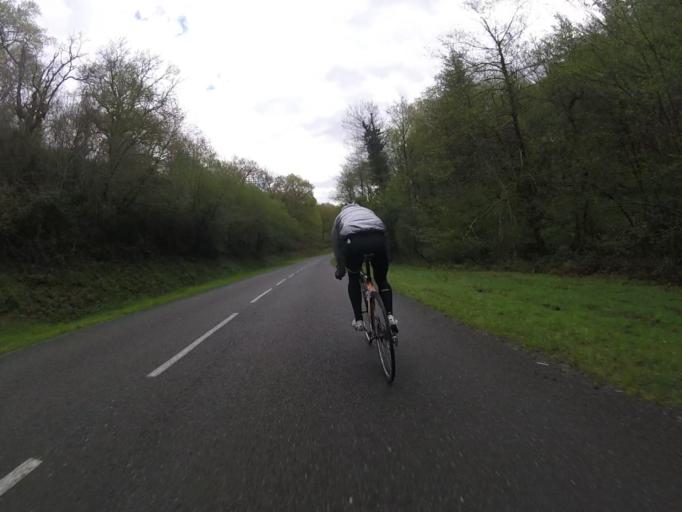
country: ES
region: Navarre
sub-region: Provincia de Navarra
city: Etxalar
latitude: 43.2844
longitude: -1.6254
